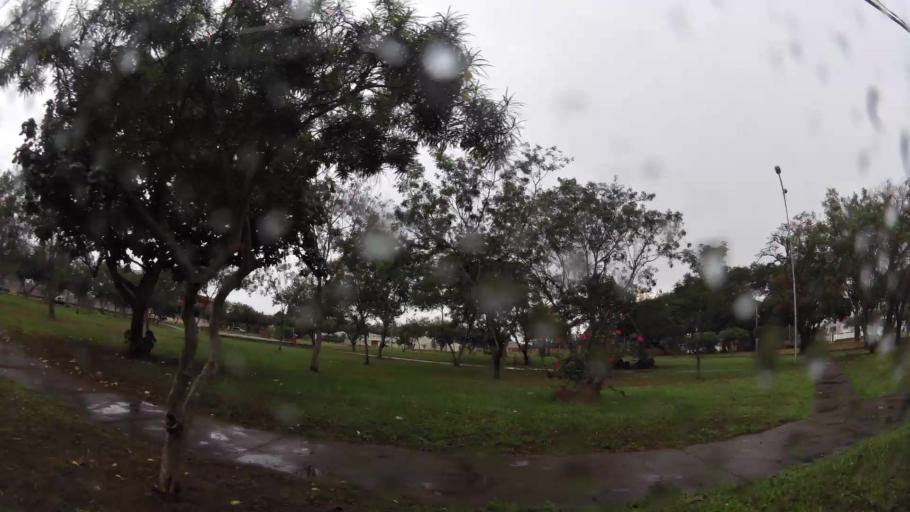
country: BO
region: Santa Cruz
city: Santa Cruz de la Sierra
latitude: -17.8065
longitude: -63.1600
